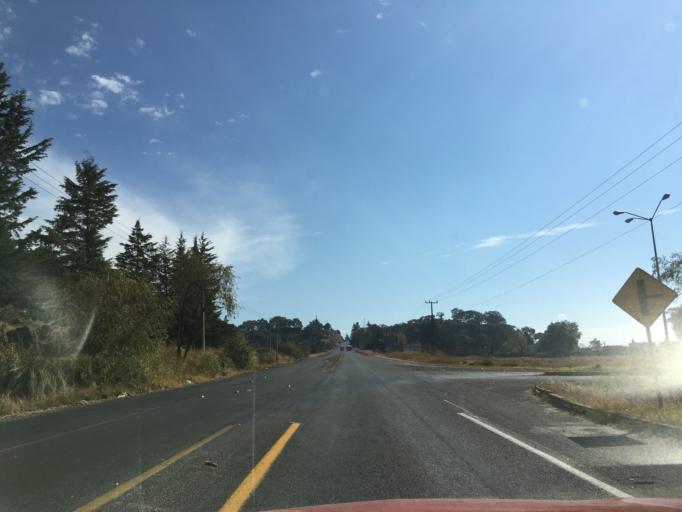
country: MX
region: Michoacan
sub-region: Hidalgo
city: Colonia Ecologica Asociacion de Lucha Social (Lucha Social)
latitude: 19.6995
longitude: -100.5888
